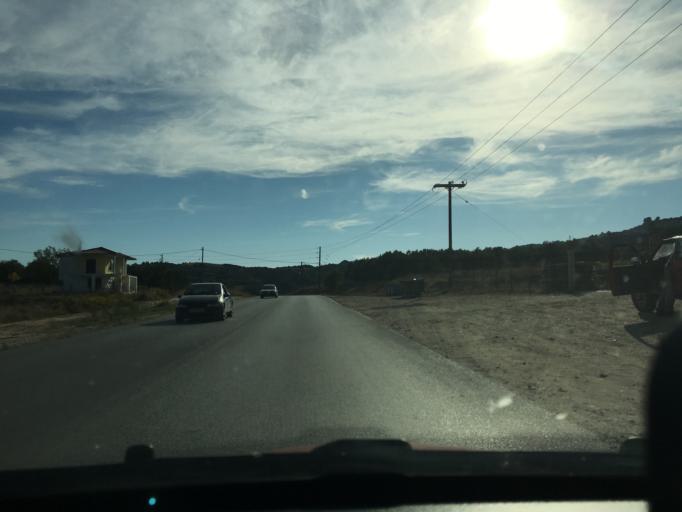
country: GR
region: Central Macedonia
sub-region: Nomos Chalkidikis
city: Agios Nikolaos
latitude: 40.2442
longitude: 23.7078
